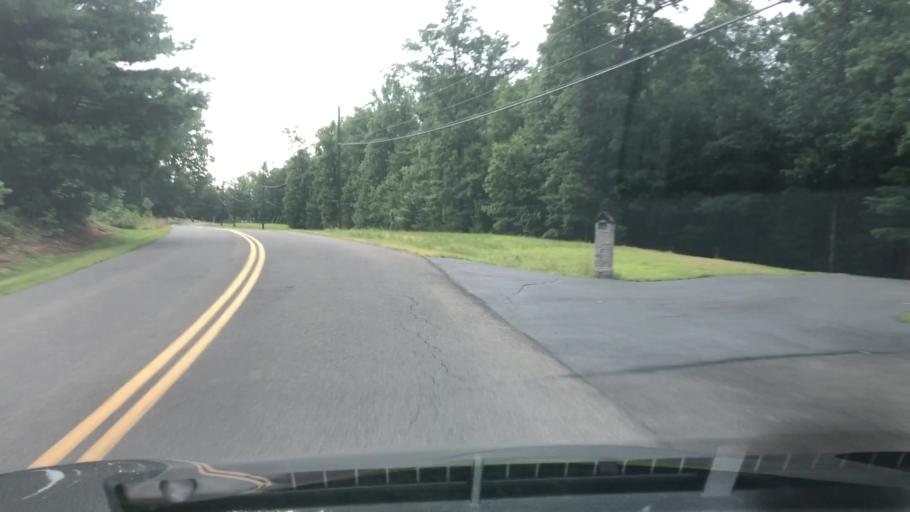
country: US
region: Virginia
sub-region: Fauquier County
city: New Baltimore
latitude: 38.7585
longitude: -77.6906
